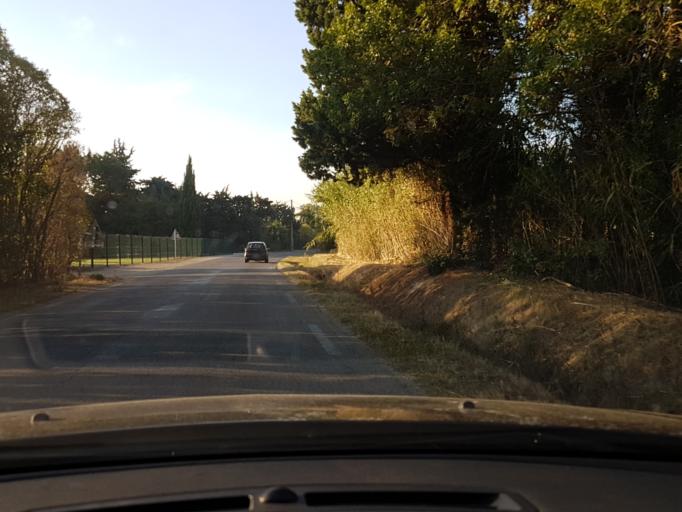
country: FR
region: Provence-Alpes-Cote d'Azur
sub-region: Departement des Bouches-du-Rhone
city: Molleges
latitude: 43.8184
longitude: 4.9481
